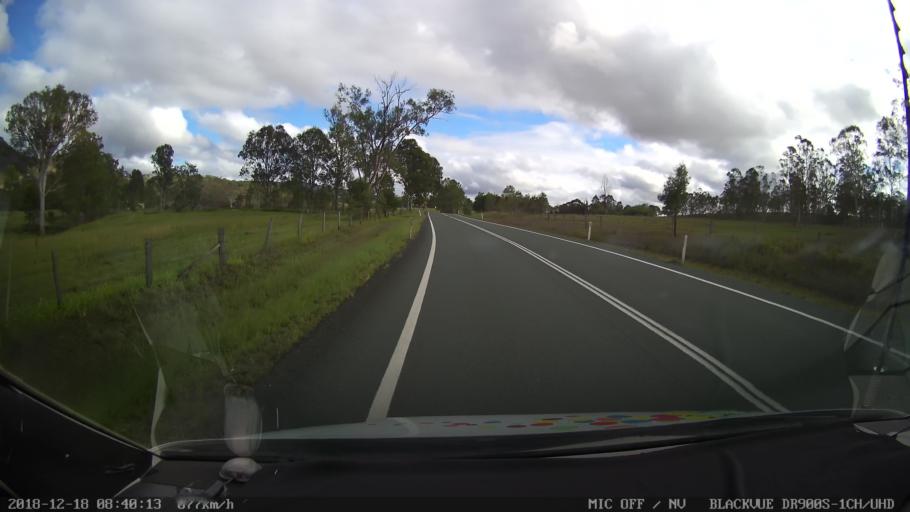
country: AU
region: Queensland
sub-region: Logan
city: Cedar Vale
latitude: -28.2445
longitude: 152.8457
